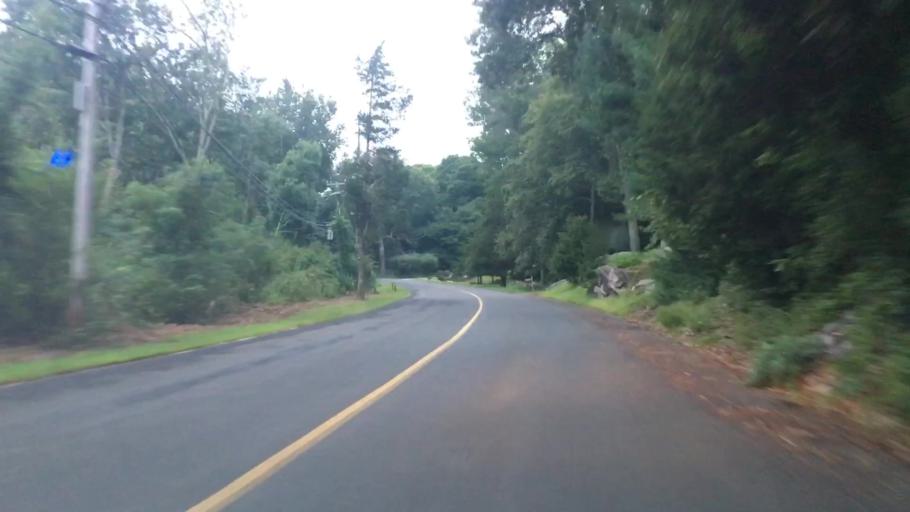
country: US
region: Connecticut
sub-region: Middlesex County
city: Essex Village
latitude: 41.3722
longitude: -72.3921
